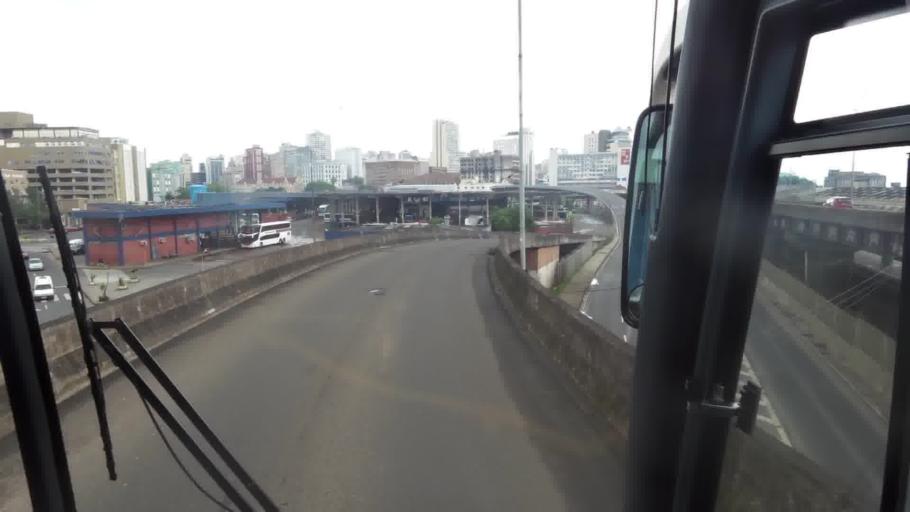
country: BR
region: Rio Grande do Sul
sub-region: Porto Alegre
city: Porto Alegre
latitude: -30.0214
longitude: -51.2182
